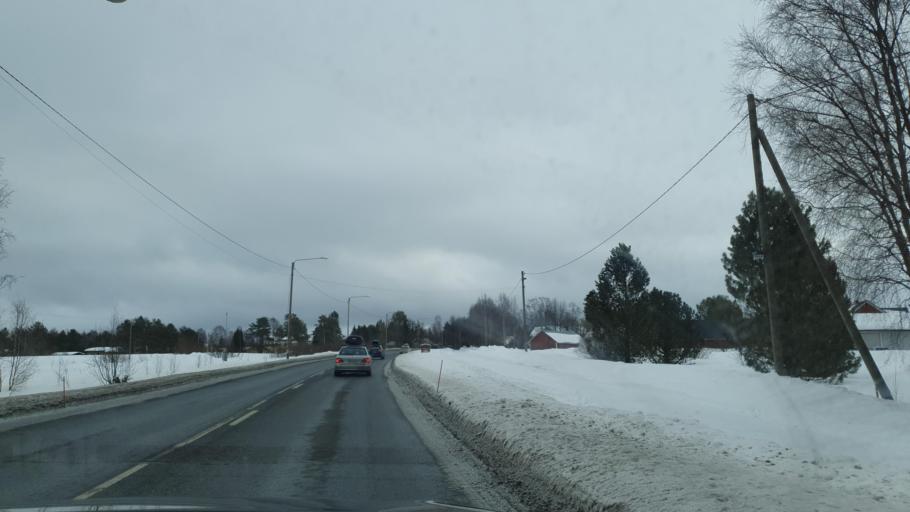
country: FI
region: Lapland
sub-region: Kemi-Tornio
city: Tornio
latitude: 65.9358
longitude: 24.1122
